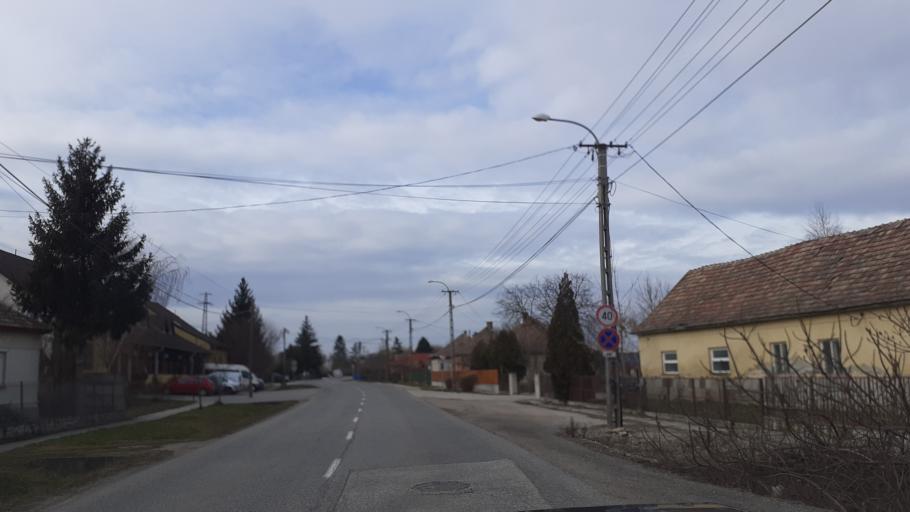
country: HU
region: Fejer
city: Szabadbattyan
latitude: 47.0796
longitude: 18.4122
